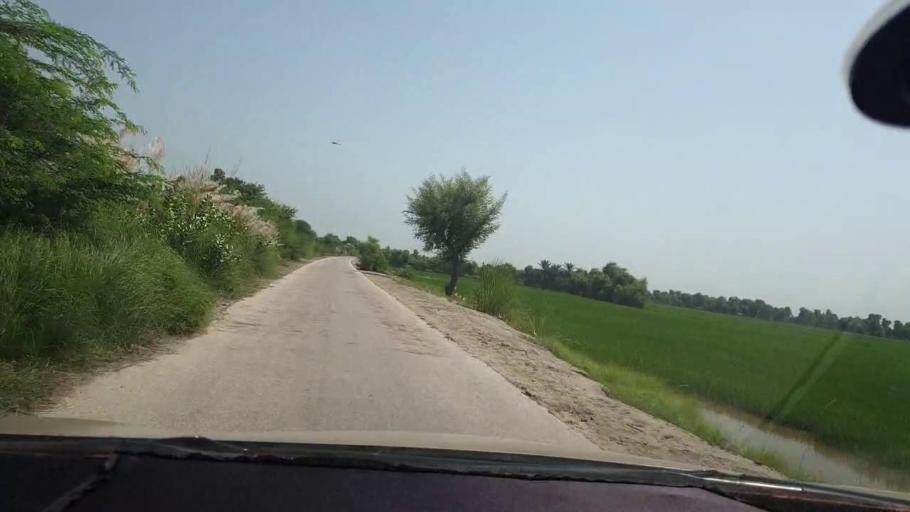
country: PK
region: Sindh
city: Kambar
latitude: 27.5148
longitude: 68.0110
